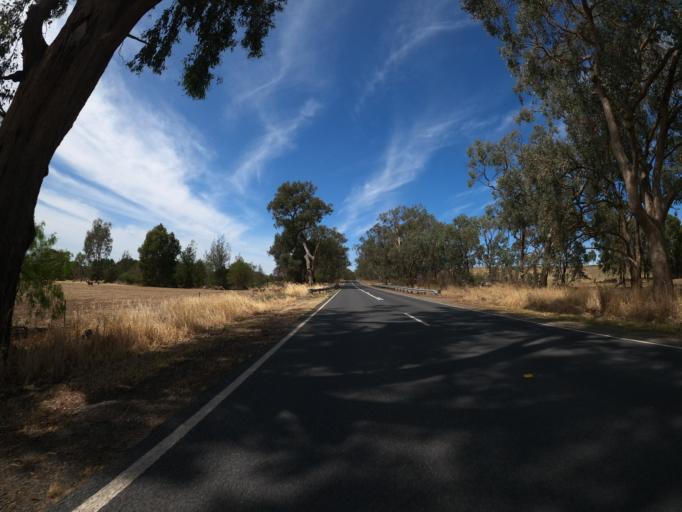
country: AU
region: Victoria
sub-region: Benalla
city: Benalla
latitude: -36.3865
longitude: 145.9793
